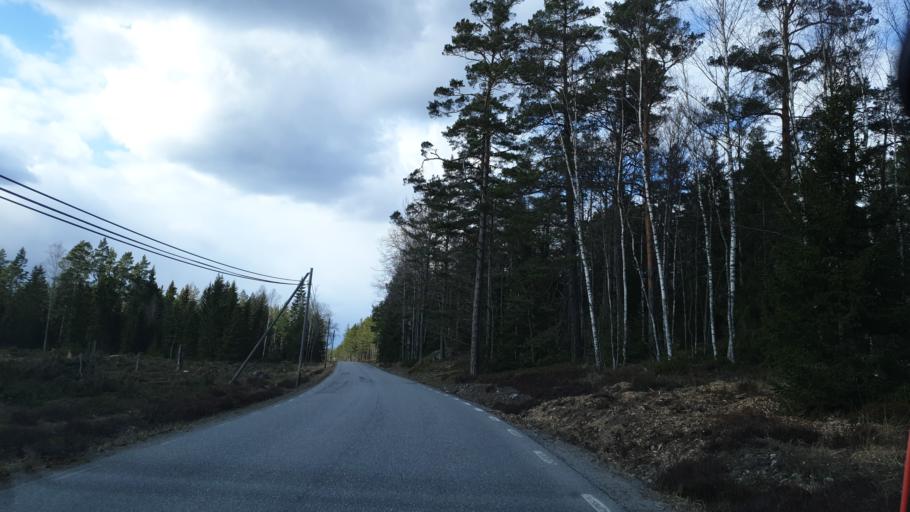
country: SE
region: Stockholm
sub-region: Tyreso Kommun
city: Brevik
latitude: 59.2496
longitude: 18.4408
